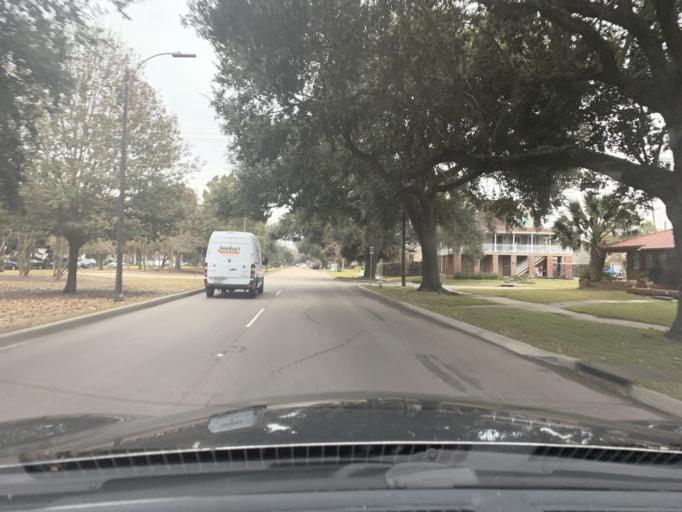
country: US
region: Louisiana
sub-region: Jefferson Parish
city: Metairie
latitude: 30.0146
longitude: -90.1071
